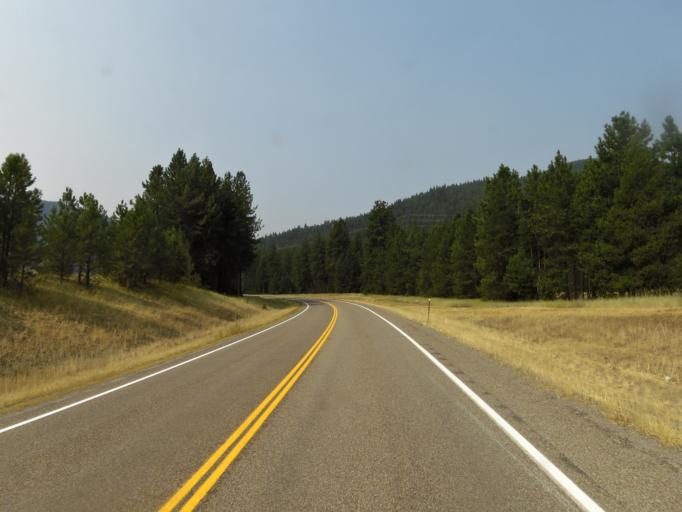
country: US
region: Montana
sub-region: Sanders County
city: Plains
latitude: 47.3396
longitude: -115.0134
